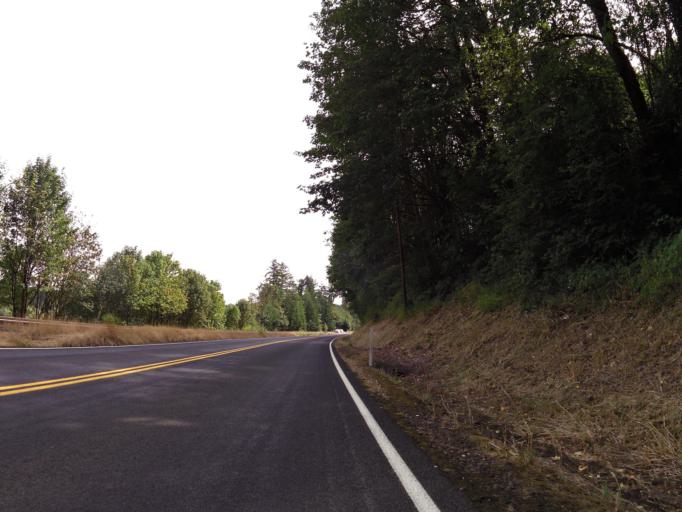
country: US
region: Washington
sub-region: Cowlitz County
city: Castle Rock
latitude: 46.3643
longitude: -122.9357
